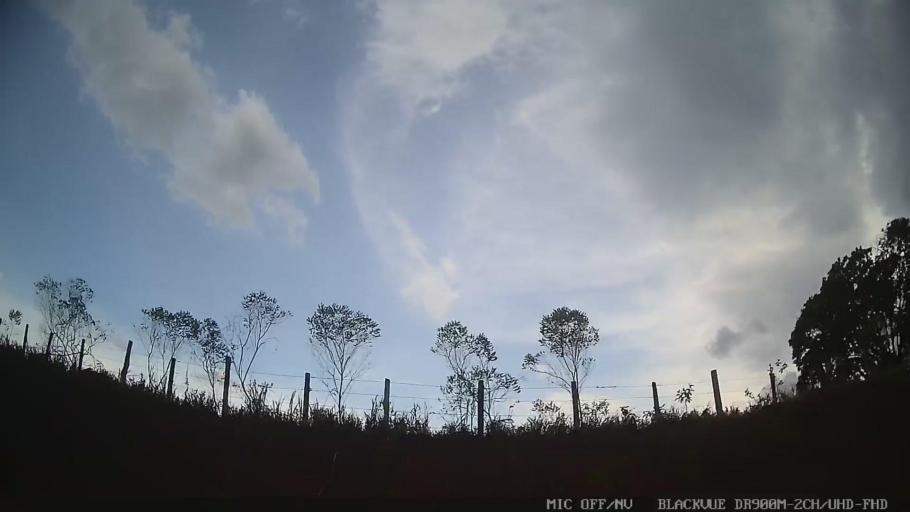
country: BR
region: Sao Paulo
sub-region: Itatiba
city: Itatiba
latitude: -22.9318
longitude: -46.7916
